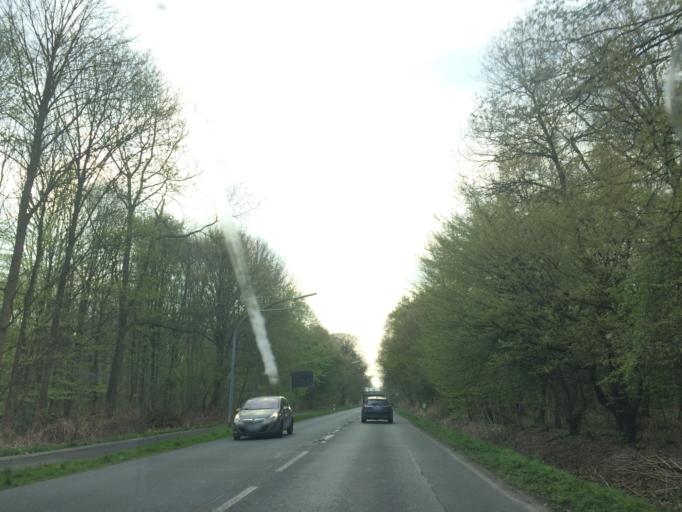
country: DE
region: North Rhine-Westphalia
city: Herten
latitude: 51.5689
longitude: 7.1268
